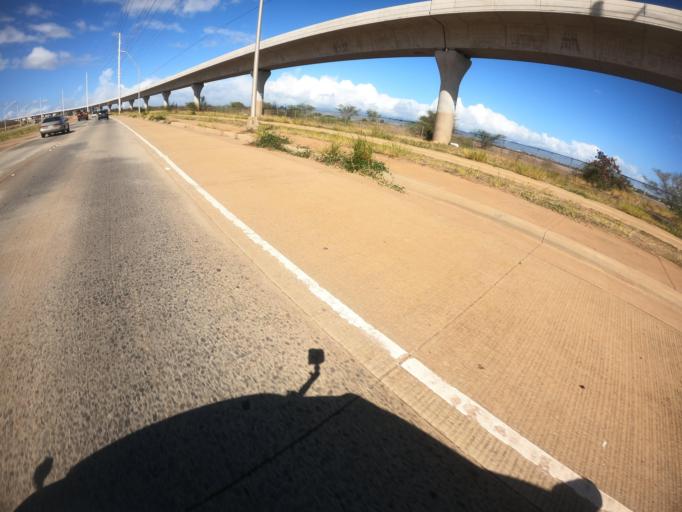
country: US
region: Hawaii
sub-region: Honolulu County
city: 'Ewa Villages
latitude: 21.3494
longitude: -158.0497
